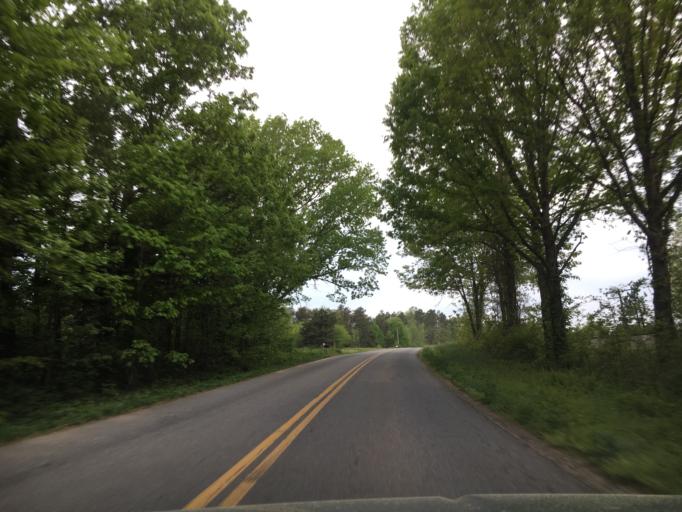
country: US
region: Virginia
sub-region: Halifax County
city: Halifax
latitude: 36.9078
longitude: -78.9326
